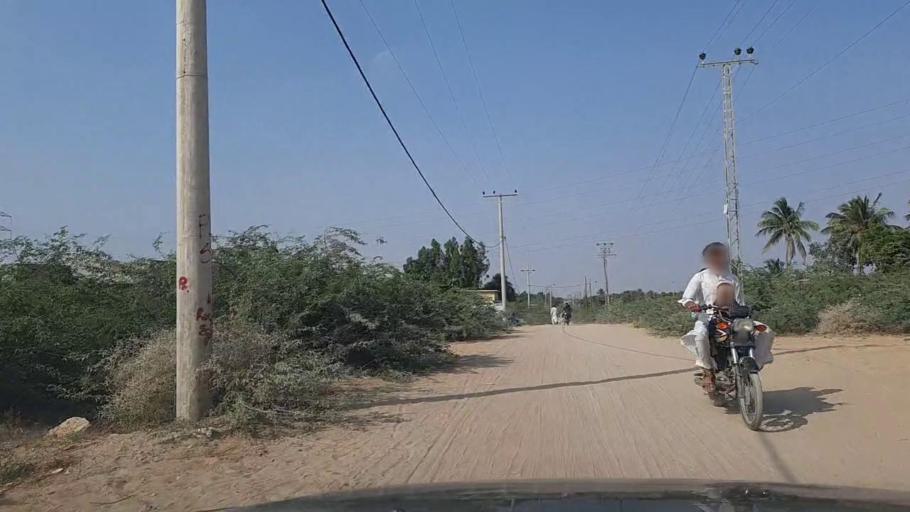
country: PK
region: Sindh
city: Gharo
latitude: 24.7473
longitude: 67.5824
